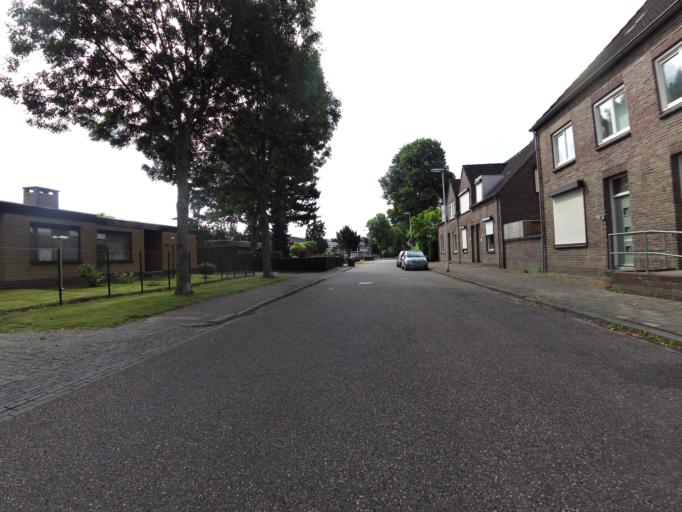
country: NL
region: Limburg
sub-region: Gemeente Heerlen
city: Mariarade
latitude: 50.9265
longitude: 5.9465
